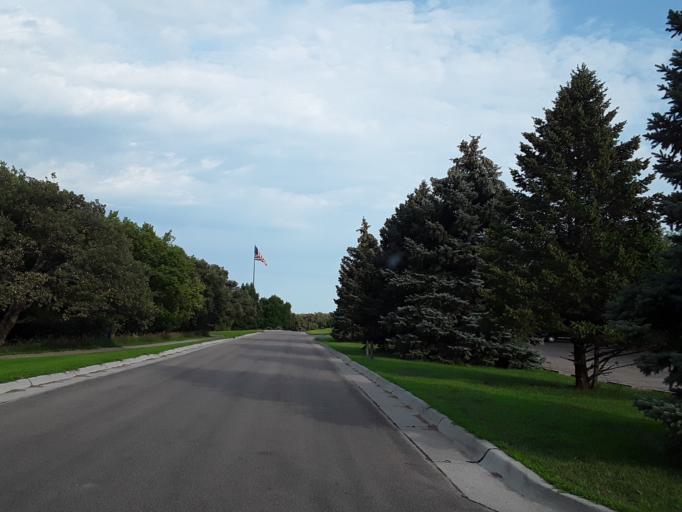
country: US
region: Nebraska
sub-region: Saunders County
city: Ashland
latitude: 41.0280
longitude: -96.3114
